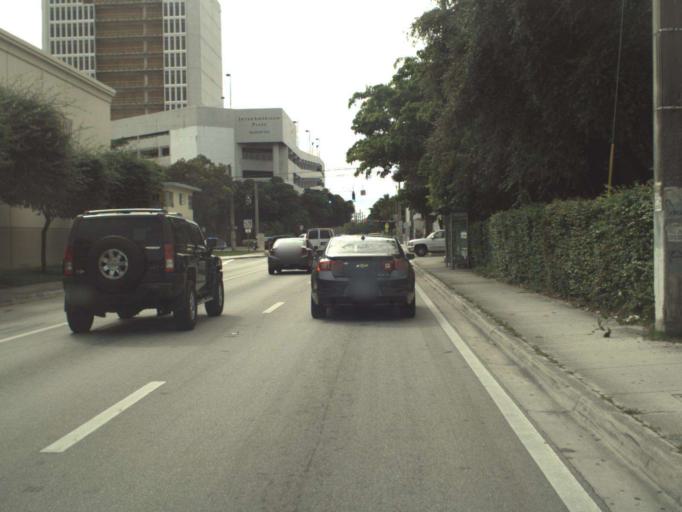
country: US
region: Florida
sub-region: Miami-Dade County
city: Miami
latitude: 25.7662
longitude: -80.2362
